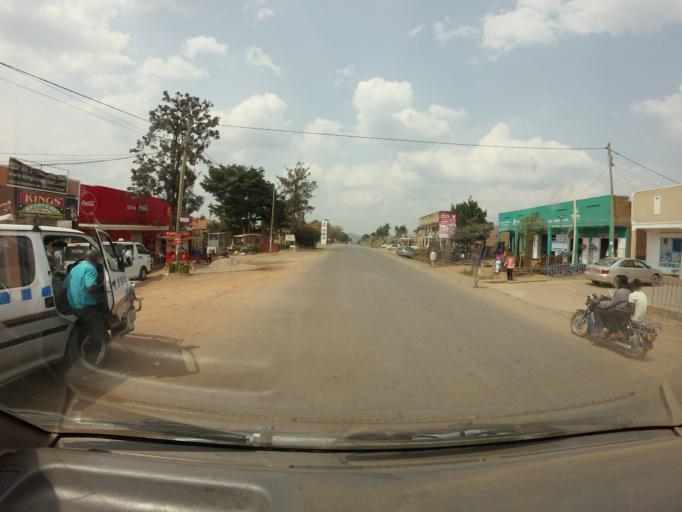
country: UG
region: Central Region
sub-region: Lyantonde District
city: Lyantonde
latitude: -0.4050
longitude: 31.1549
